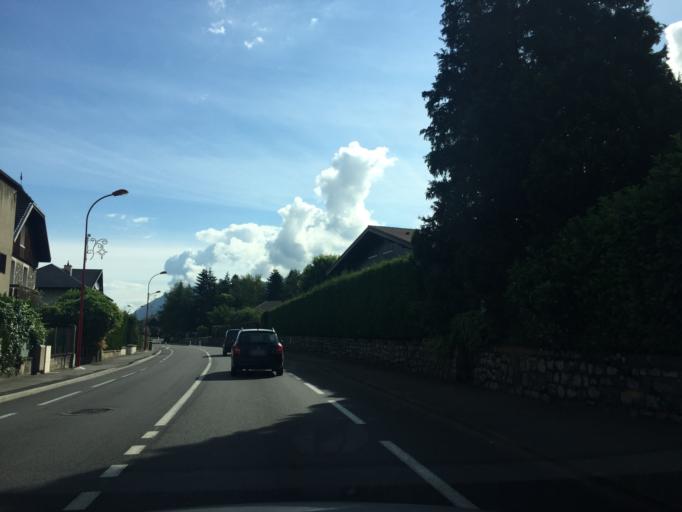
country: FR
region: Rhone-Alpes
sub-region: Departement de la Savoie
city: La Rochette
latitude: 45.4535
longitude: 6.1112
